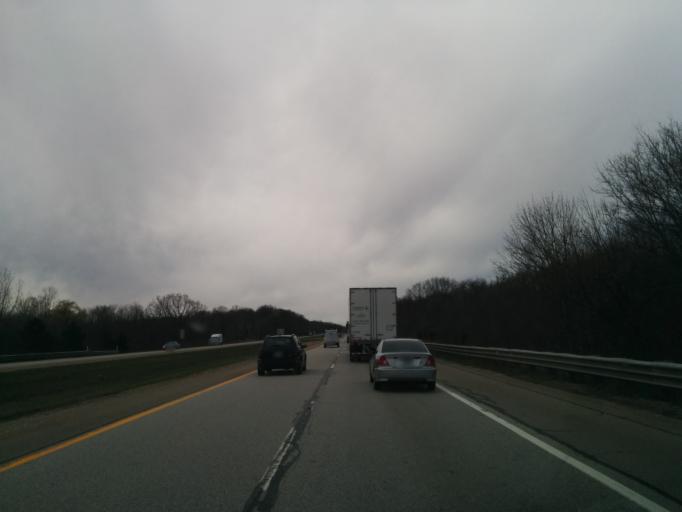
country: US
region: Michigan
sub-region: Ottawa County
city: Jenison
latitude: 42.8765
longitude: -85.7837
